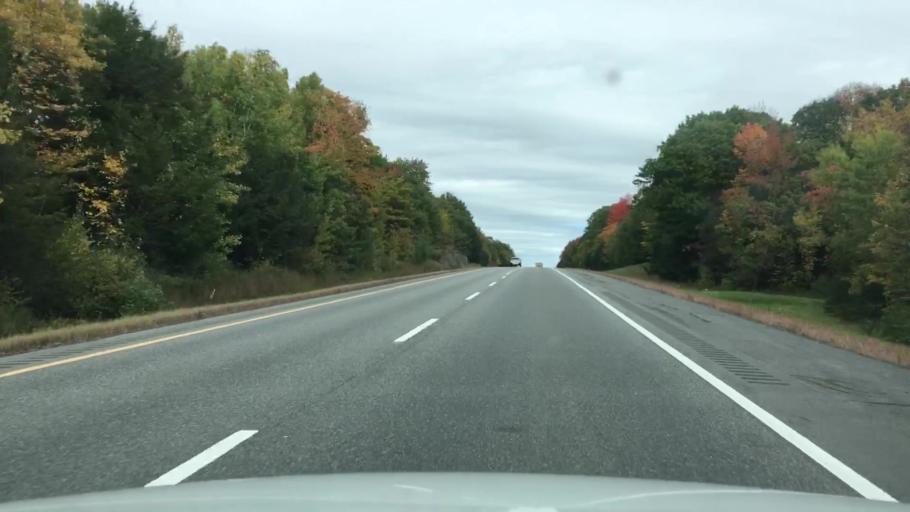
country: US
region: Maine
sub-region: Kennebec County
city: Sidney
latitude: 44.4026
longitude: -69.7513
